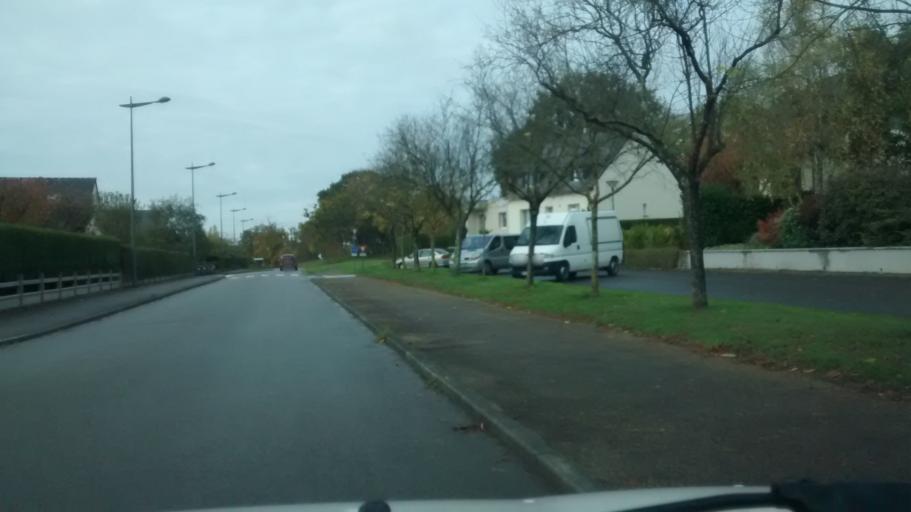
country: FR
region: Brittany
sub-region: Departement d'Ille-et-Vilaine
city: Chateaubourg
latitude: 48.1131
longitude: -1.3875
